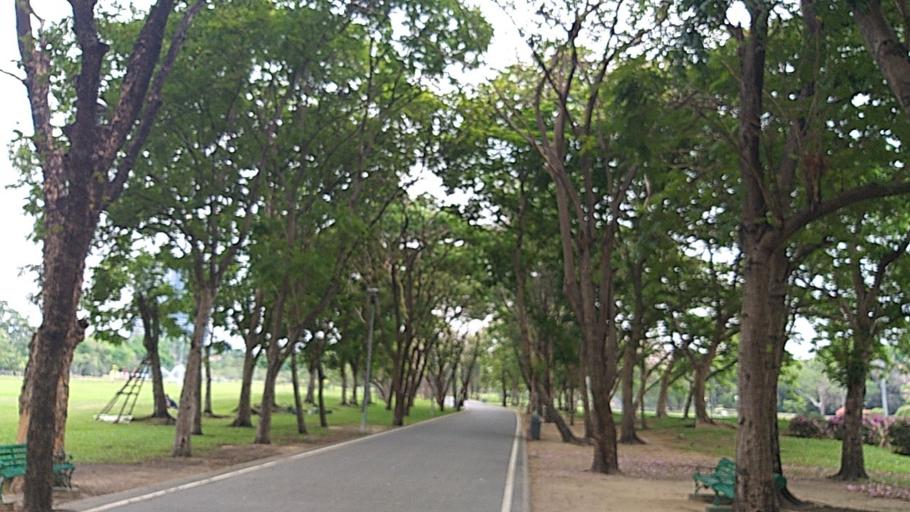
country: TH
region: Bangkok
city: Chatuchak
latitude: 13.8140
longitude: 100.5537
